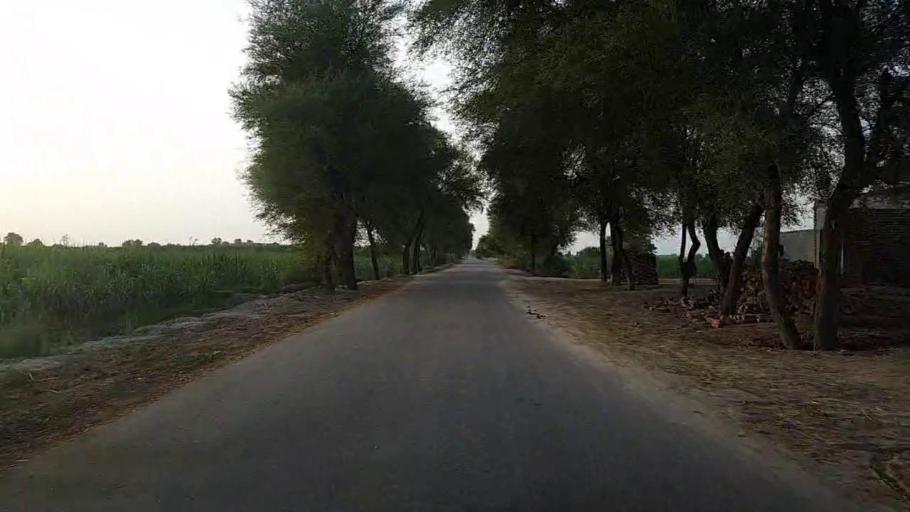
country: PK
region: Sindh
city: Ubauro
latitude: 28.2472
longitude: 69.8093
